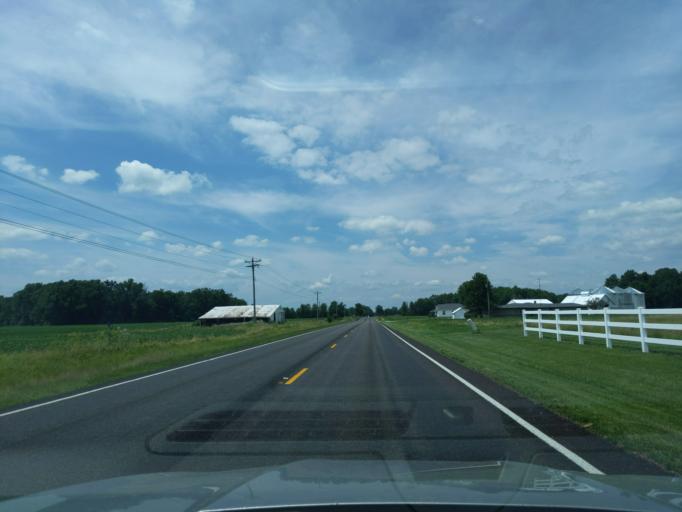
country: US
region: Indiana
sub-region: Decatur County
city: Greensburg
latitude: 39.2703
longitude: -85.3898
